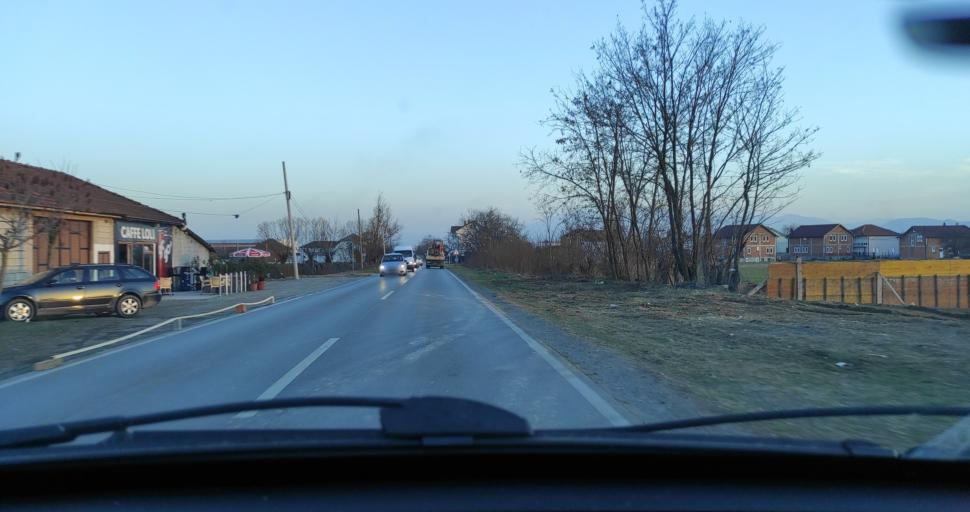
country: XK
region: Gjakova
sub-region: Komuna e Gjakoves
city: Gjakove
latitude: 42.4202
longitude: 20.3947
